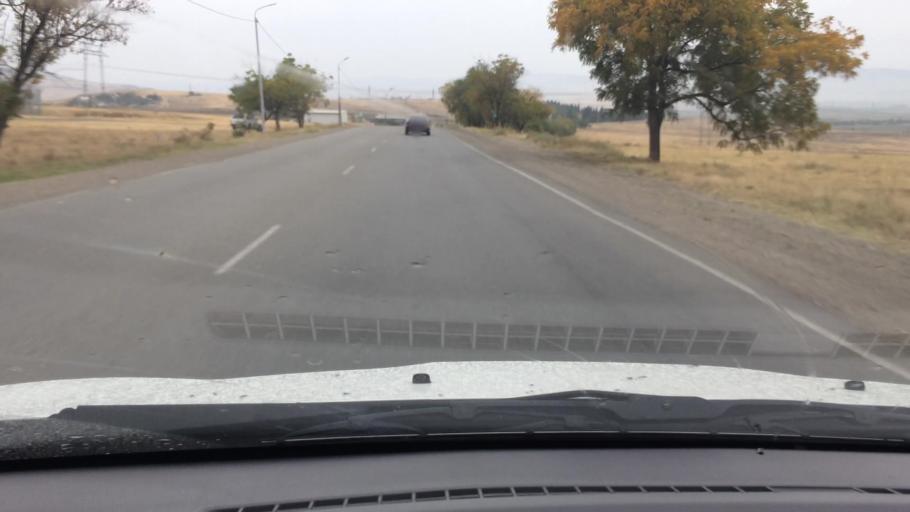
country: GE
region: Kvemo Kartli
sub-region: Marneuli
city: Marneuli
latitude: 41.5162
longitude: 44.7848
